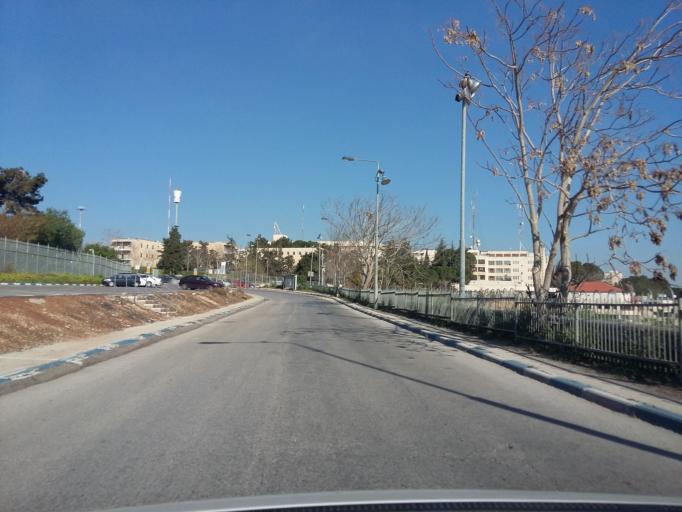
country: PS
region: West Bank
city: East Jerusalem
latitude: 31.7950
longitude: 35.2442
